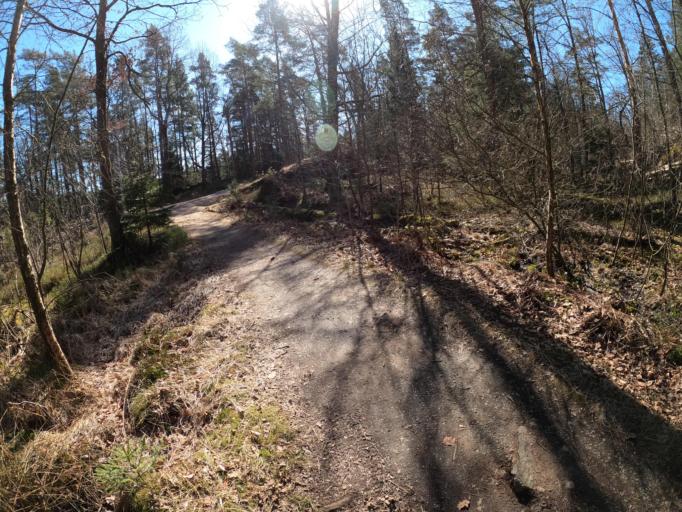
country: SE
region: Vaestra Goetaland
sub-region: Harryda Kommun
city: Molnlycke
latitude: 57.6393
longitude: 12.1289
